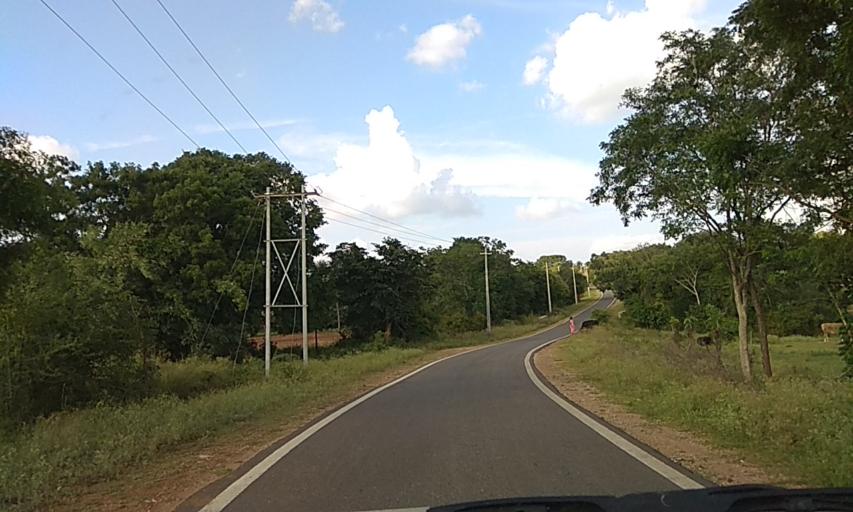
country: IN
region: Karnataka
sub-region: Chamrajnagar
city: Gundlupet
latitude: 11.7664
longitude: 76.7805
